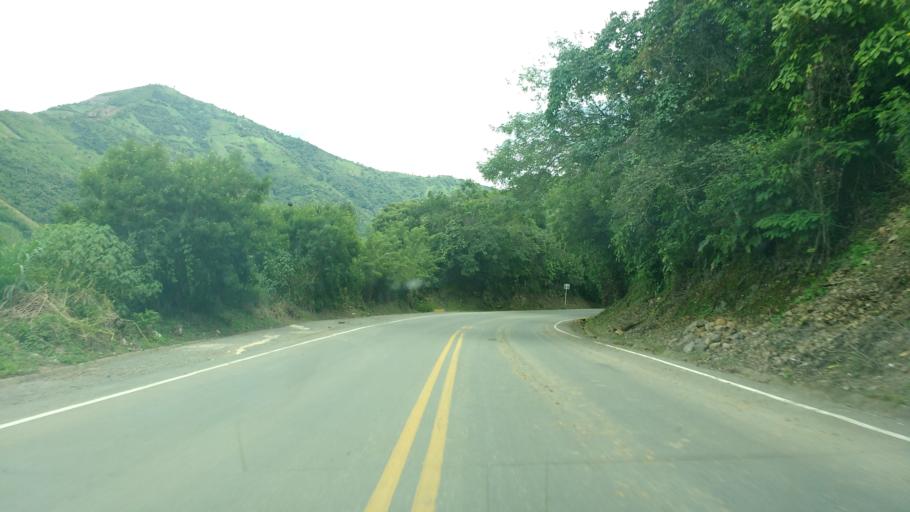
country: CO
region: Antioquia
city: Titiribi
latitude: 6.0619
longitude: -75.7472
